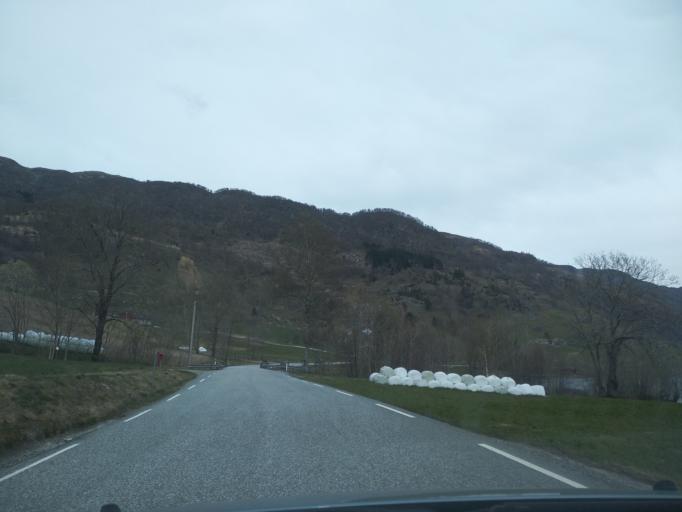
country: NO
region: Hordaland
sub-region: Etne
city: Etne
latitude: 59.6862
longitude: 6.0097
